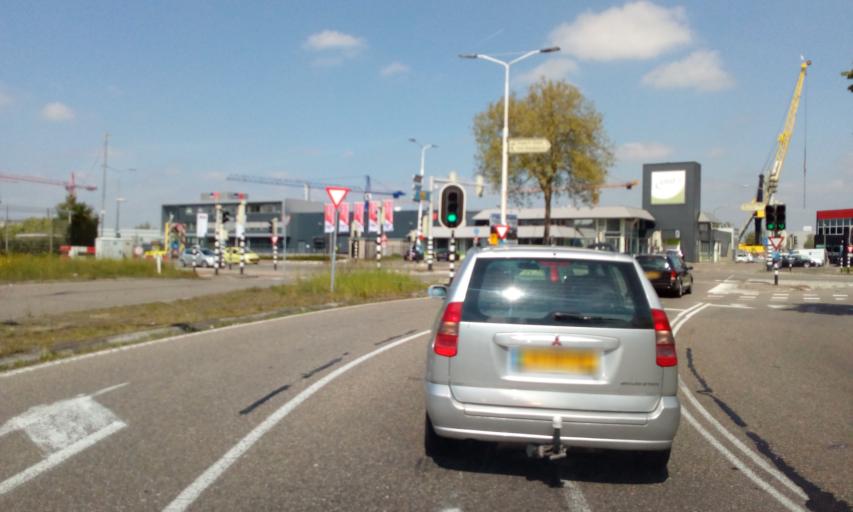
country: NL
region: South Holland
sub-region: Gemeente Papendrecht
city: Papendrecht
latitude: 51.8166
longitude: 4.7056
